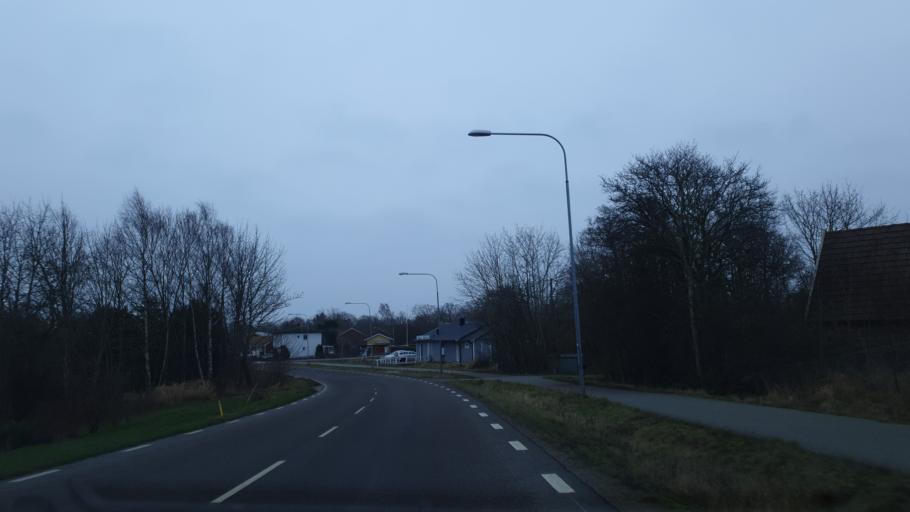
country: SE
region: Blekinge
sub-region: Karlskrona Kommun
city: Sturko
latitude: 56.1137
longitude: 15.6743
